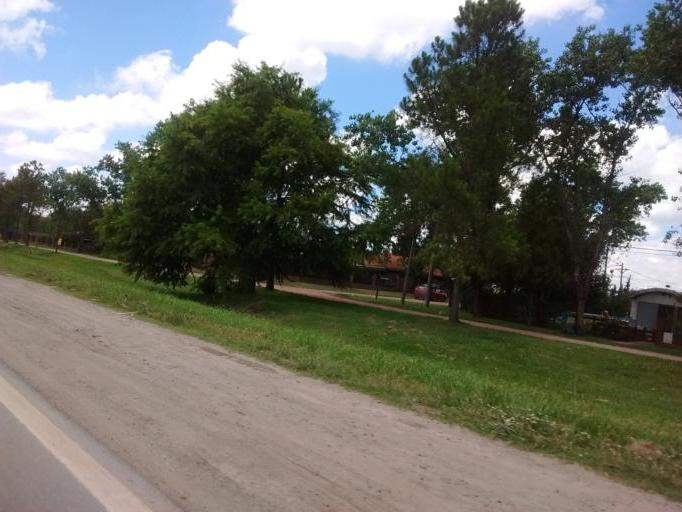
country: AR
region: Santa Fe
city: Funes
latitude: -32.9233
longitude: -60.7957
